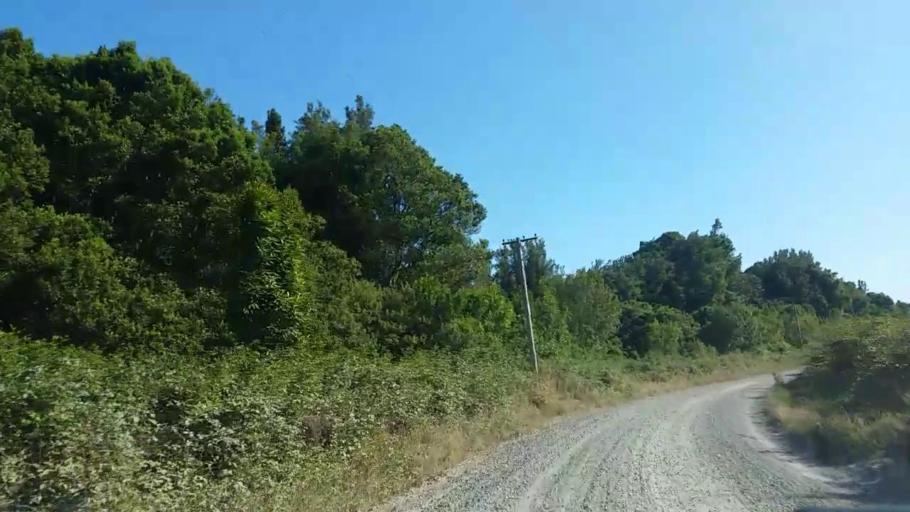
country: NZ
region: Bay of Plenty
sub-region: Kawerau District
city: Kawerau
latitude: -38.0119
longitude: 176.4898
